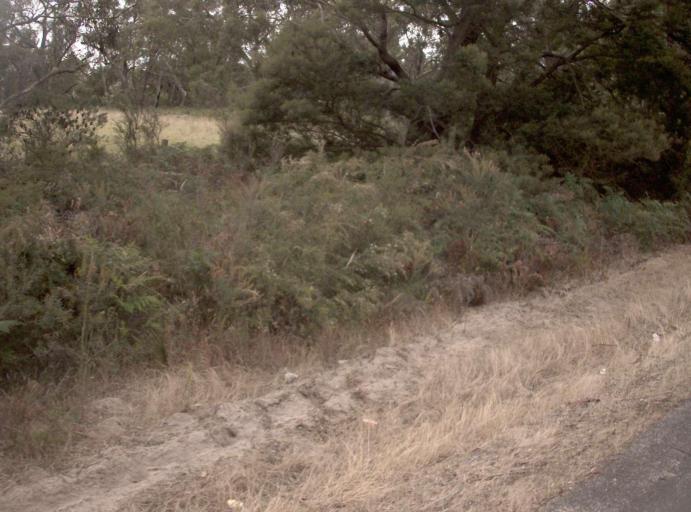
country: AU
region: Victoria
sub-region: Wellington
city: Sale
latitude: -38.2726
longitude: 147.0355
